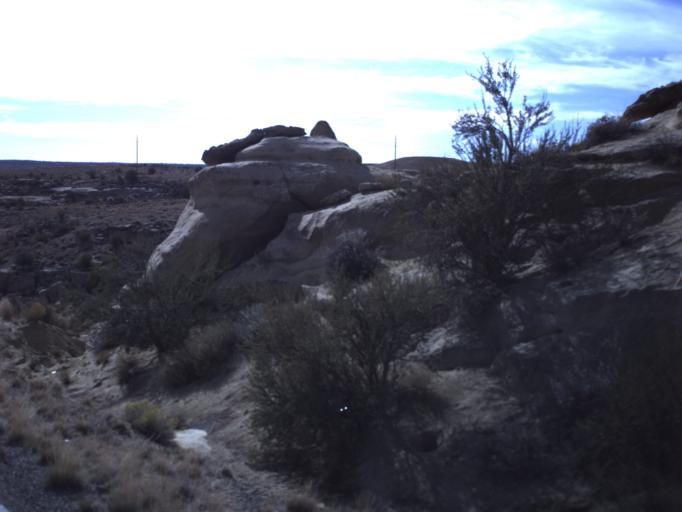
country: US
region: Utah
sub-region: San Juan County
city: Blanding
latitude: 37.4187
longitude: -109.4546
